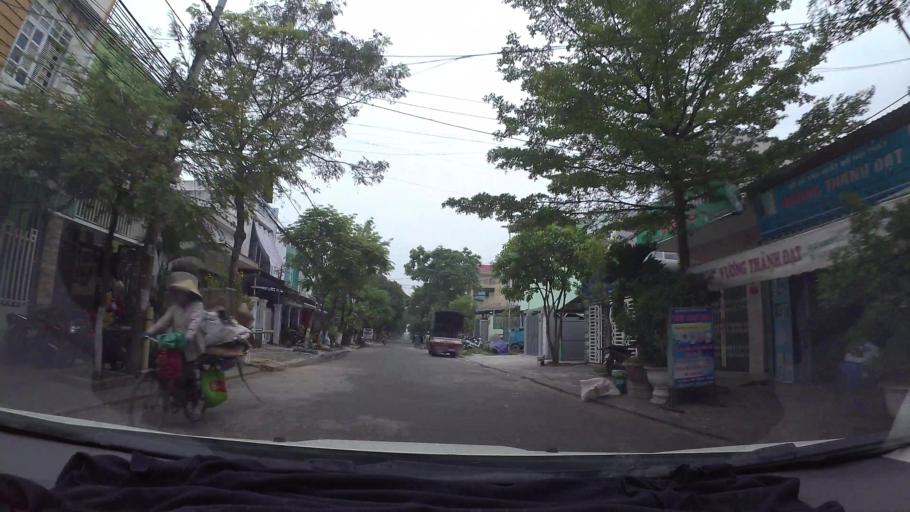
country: VN
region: Da Nang
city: Thanh Khe
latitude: 16.0516
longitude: 108.1788
